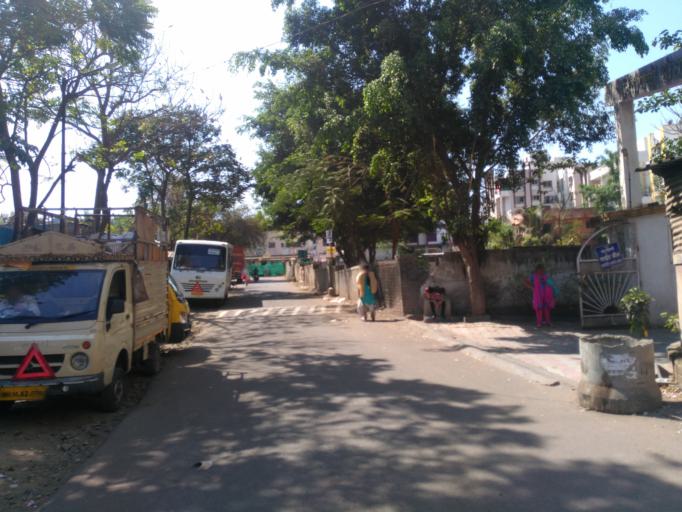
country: IN
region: Maharashtra
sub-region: Pune Division
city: Pune
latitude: 18.4486
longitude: 73.8765
